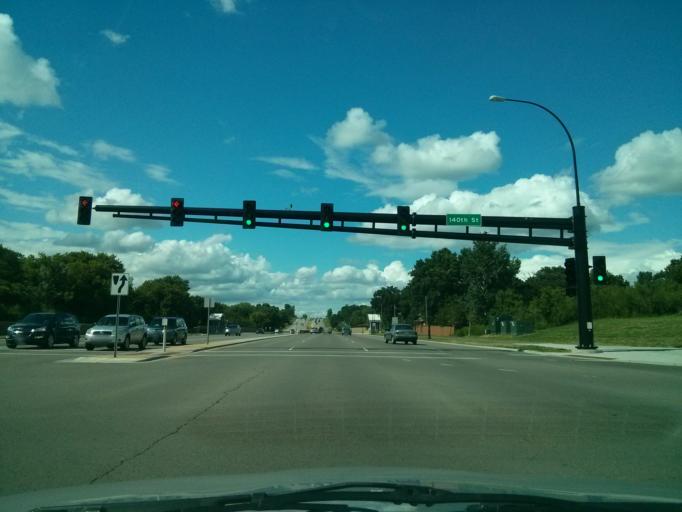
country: US
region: Minnesota
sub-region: Dakota County
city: Apple Valley
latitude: 44.7465
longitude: -93.2176
